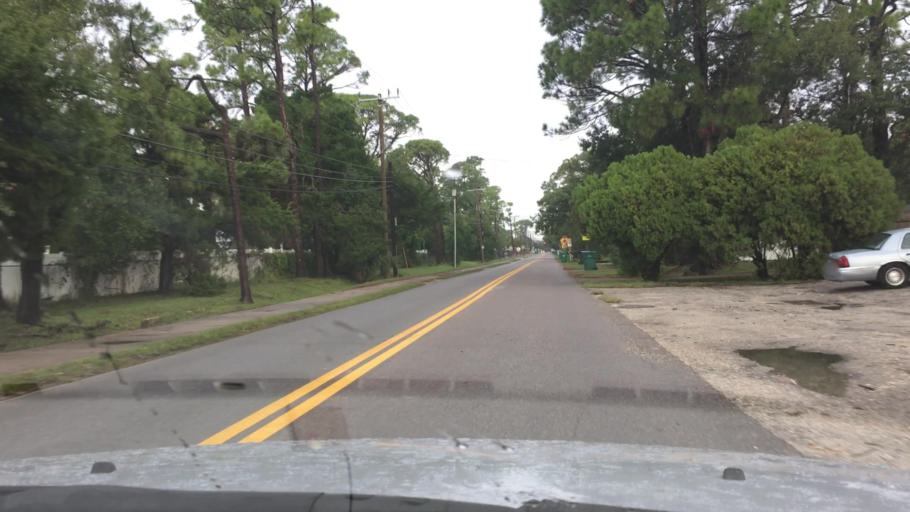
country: US
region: Florida
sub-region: Volusia County
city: Holly Hill
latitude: 29.2473
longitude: -81.0529
